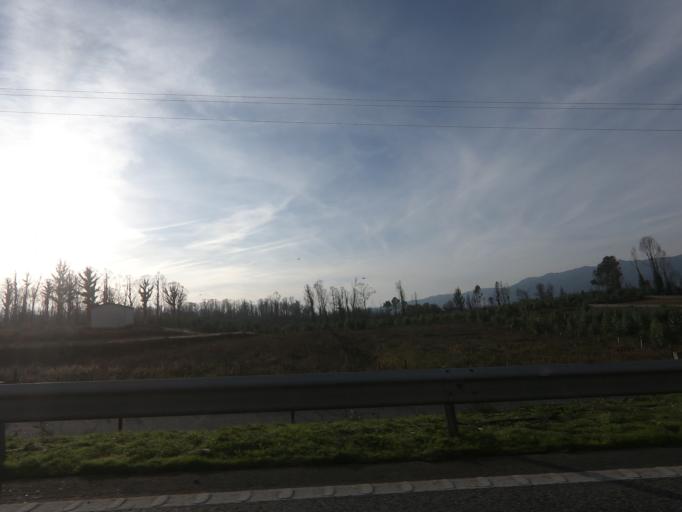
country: PT
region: Viseu
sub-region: Concelho de Tondela
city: Tondela
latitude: 40.5061
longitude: -8.0849
